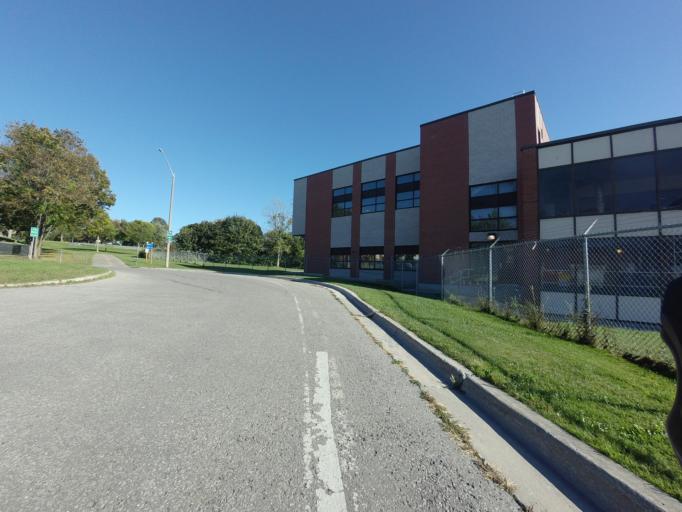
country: CA
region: Ontario
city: Oshawa
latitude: 43.8594
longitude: -78.8356
